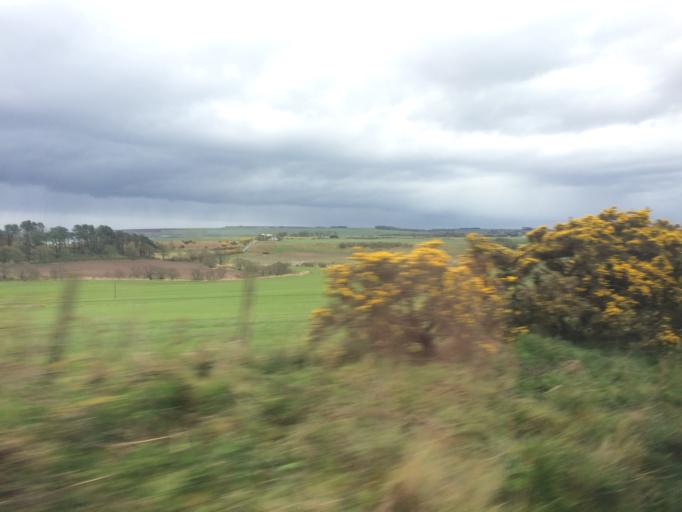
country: GB
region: Scotland
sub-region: Angus
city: Montrose
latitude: 56.6555
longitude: -2.5186
